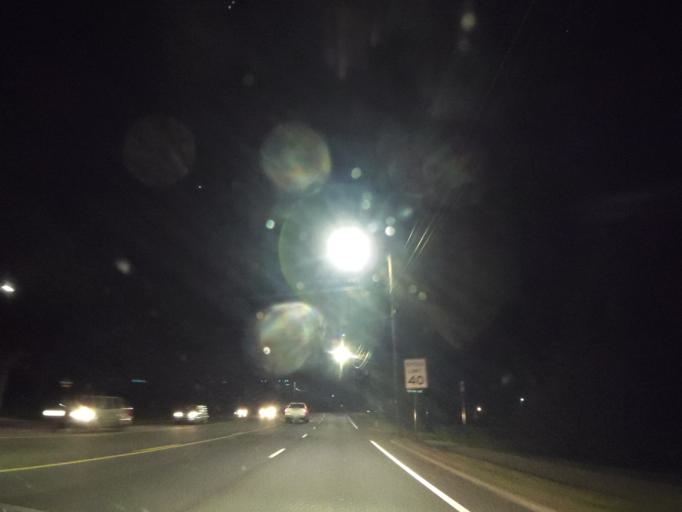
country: US
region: Georgia
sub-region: Whitfield County
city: Dalton
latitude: 34.7616
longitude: -84.9772
